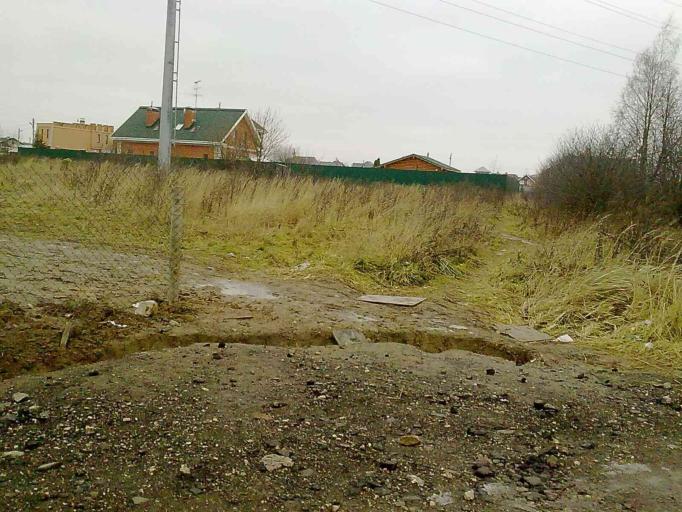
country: RU
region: Moskovskaya
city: Gorki Vtoryye
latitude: 55.6756
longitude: 37.1490
